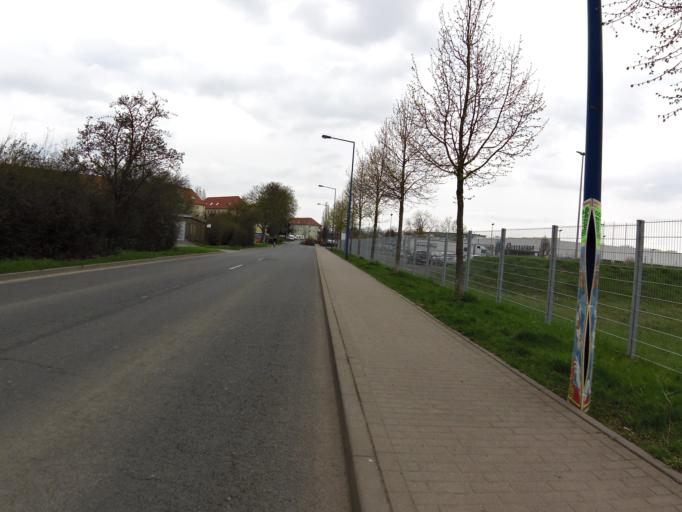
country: DE
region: Thuringia
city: Gotha
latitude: 50.9563
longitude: 10.7186
